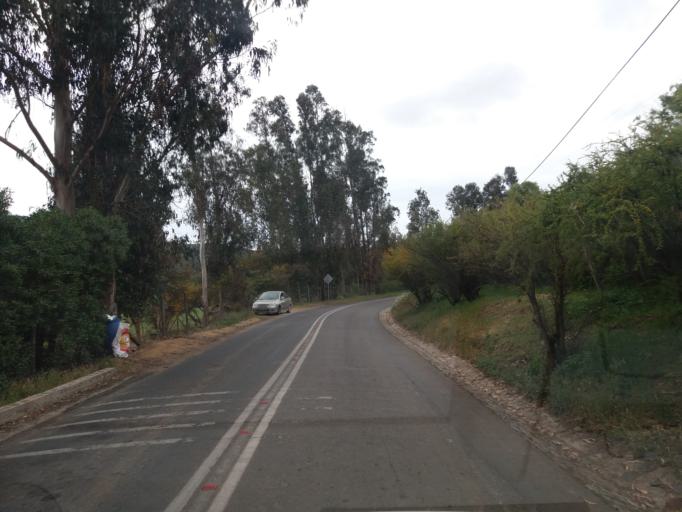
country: CL
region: Valparaiso
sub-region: Provincia de Quillota
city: Quillota
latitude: -32.8910
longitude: -71.3079
